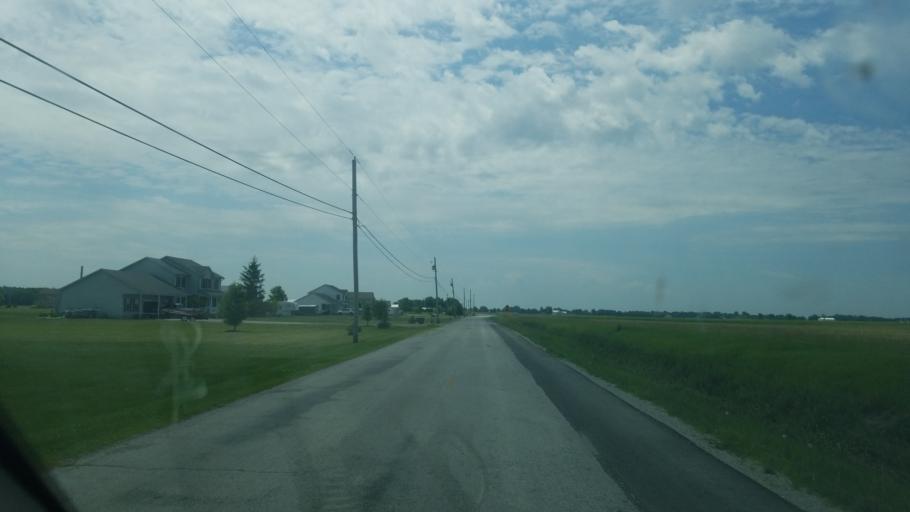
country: US
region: Ohio
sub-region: Wood County
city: Bowling Green
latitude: 41.2853
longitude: -83.5927
